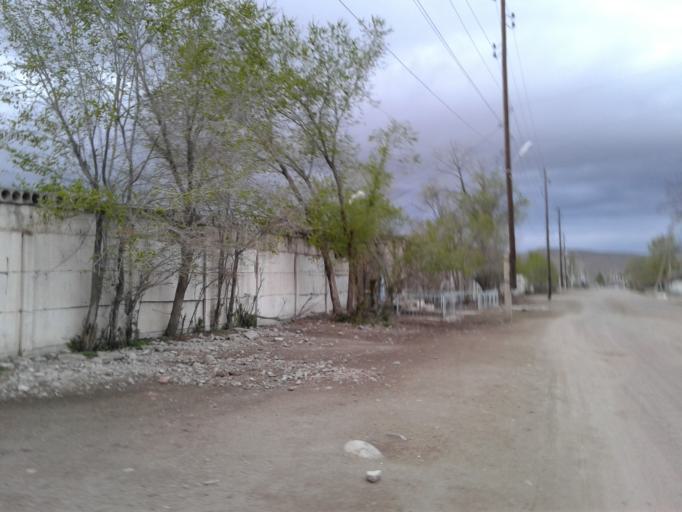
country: KG
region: Ysyk-Koel
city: Bokombayevskoye
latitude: 42.1176
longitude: 76.9879
